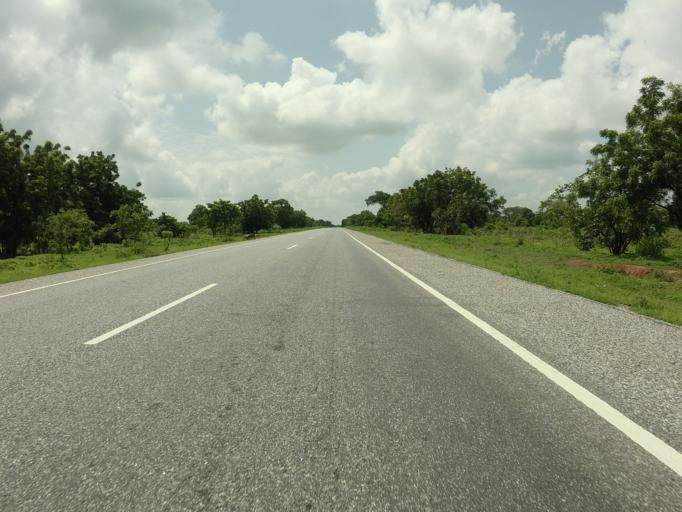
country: GH
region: Northern
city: Tamale
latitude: 9.1512
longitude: -1.3908
